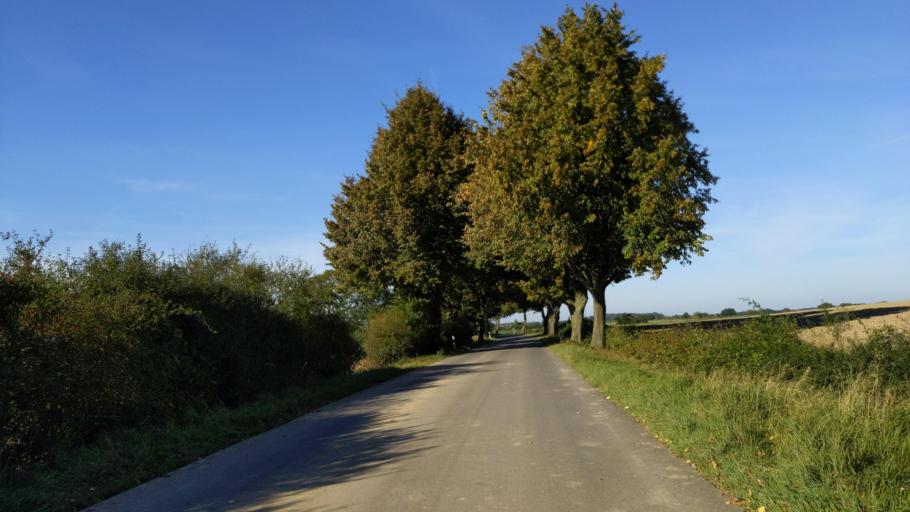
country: DE
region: Schleswig-Holstein
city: Ahrensbok
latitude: 54.0233
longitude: 10.6187
